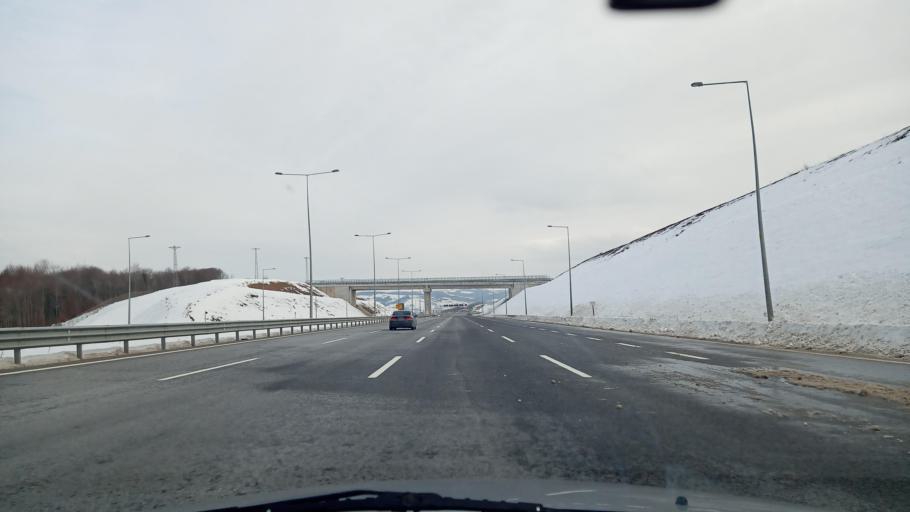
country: TR
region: Kocaeli
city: Korfez
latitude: 40.8894
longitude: 29.7209
